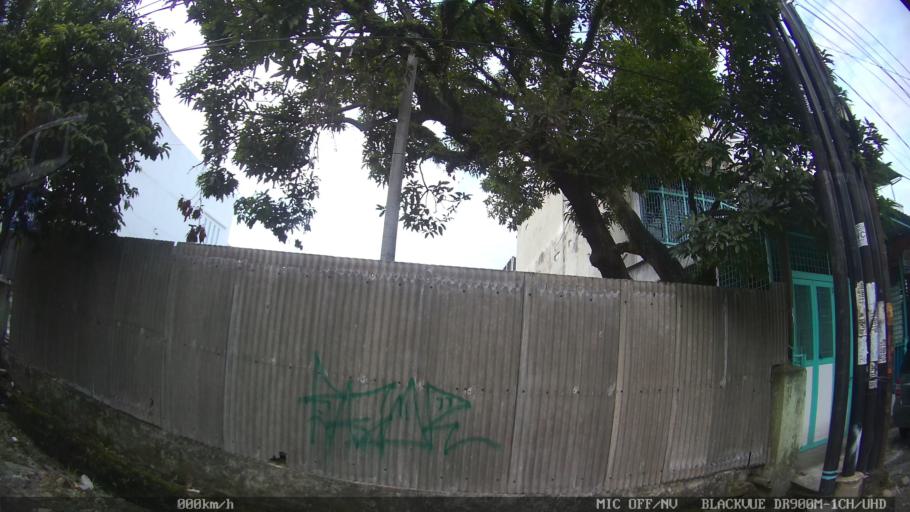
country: ID
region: North Sumatra
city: Medan
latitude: 3.6073
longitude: 98.6792
